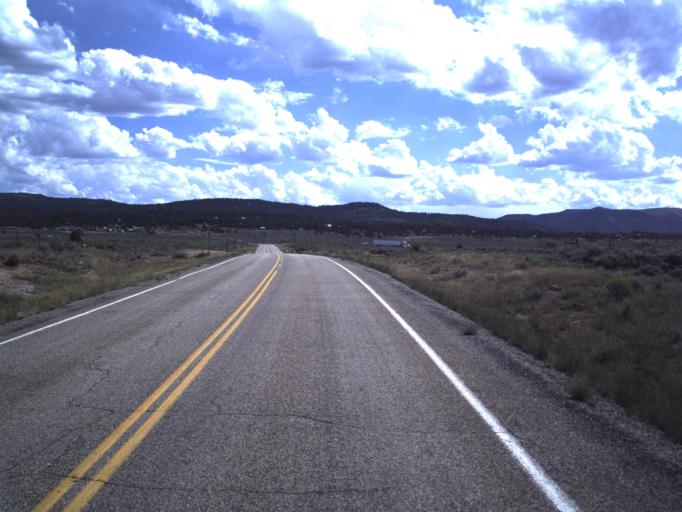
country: US
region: Utah
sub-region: Duchesne County
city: Duchesne
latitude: 40.2110
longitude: -110.7294
